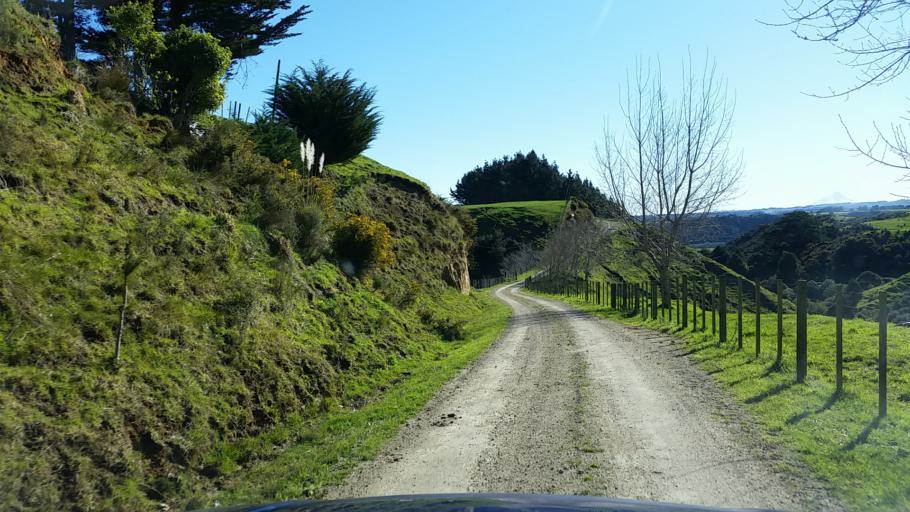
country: NZ
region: Taranaki
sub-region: South Taranaki District
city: Patea
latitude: -39.7923
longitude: 174.7733
